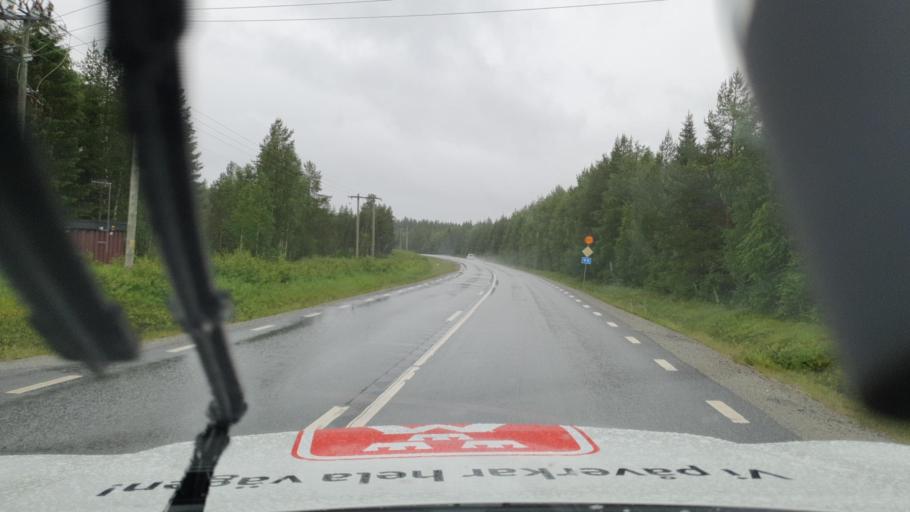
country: SE
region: Vaesterbotten
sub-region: Lycksele Kommun
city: Lycksele
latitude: 64.0773
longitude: 18.3399
